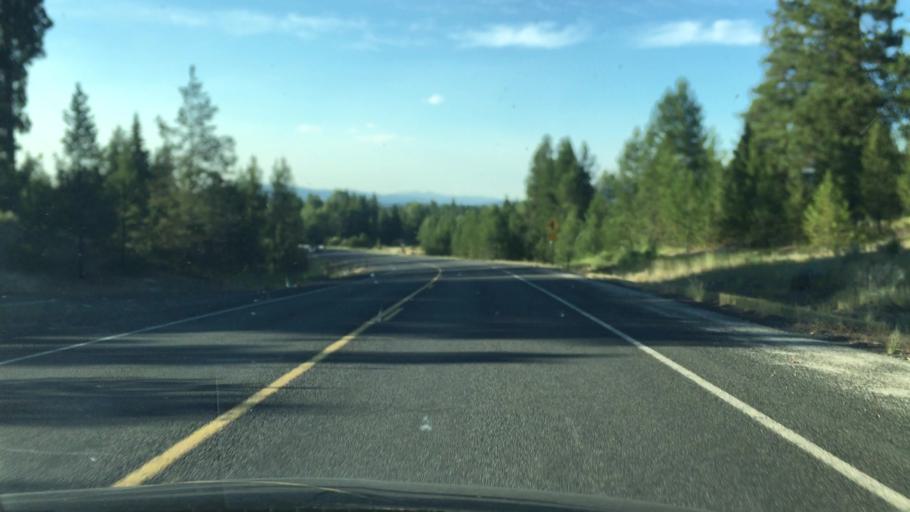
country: US
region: Idaho
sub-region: Valley County
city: McCall
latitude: 44.7858
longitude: -116.0765
